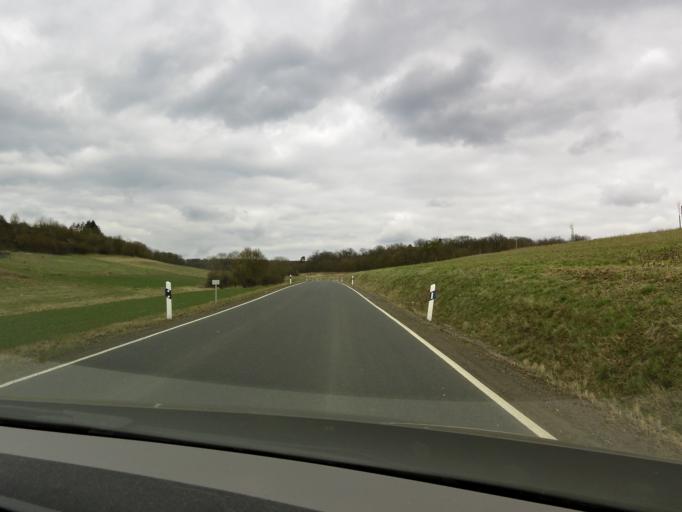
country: DE
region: Bavaria
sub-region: Regierungsbezirk Unterfranken
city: Rimpar
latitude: 49.8644
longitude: 9.9676
